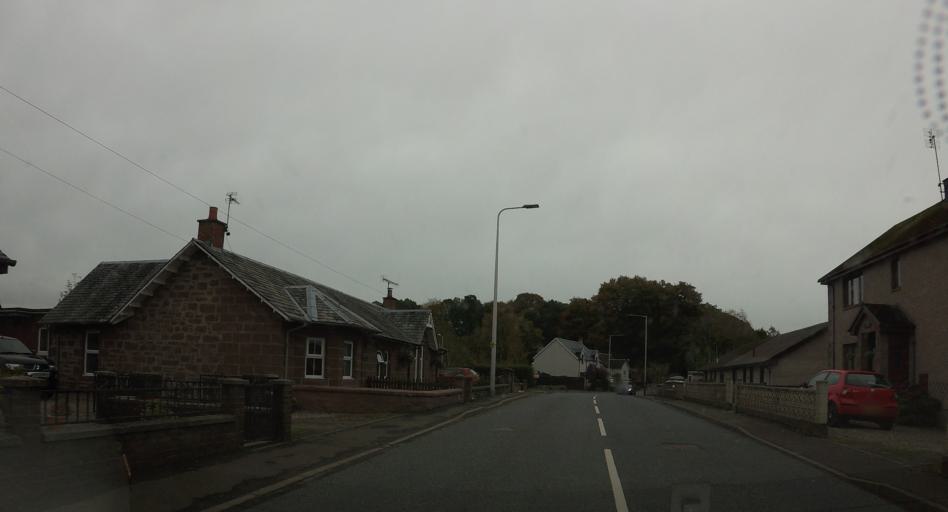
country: GB
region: Scotland
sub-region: Perth and Kinross
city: Stanley
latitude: 56.5514
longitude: -3.4507
